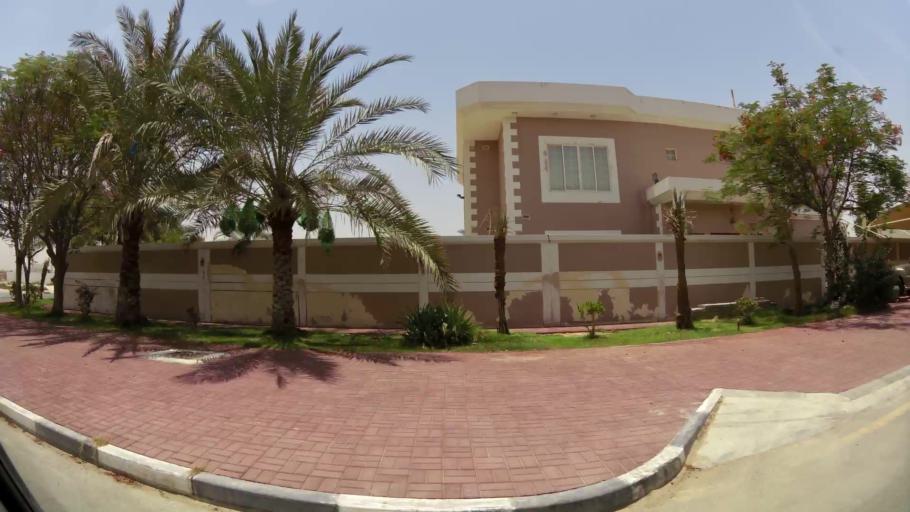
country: AE
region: Ash Shariqah
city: Sharjah
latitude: 25.2399
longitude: 55.4597
